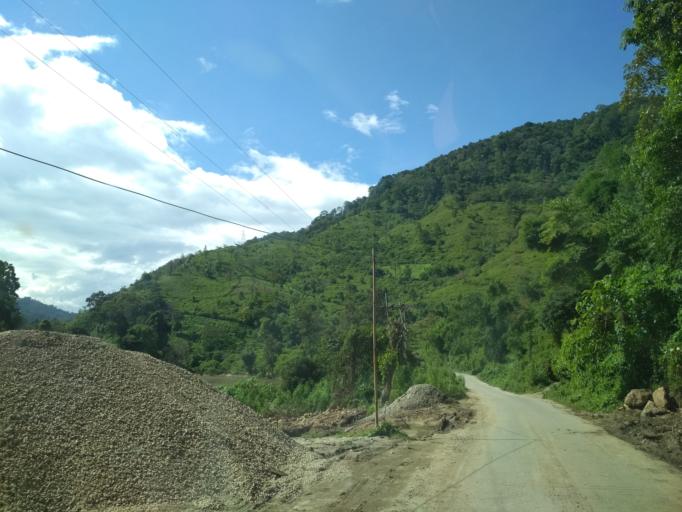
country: IN
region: Arunachal Pradesh
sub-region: Lower Subansiri
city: Ziro
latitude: 27.3609
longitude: 93.7788
